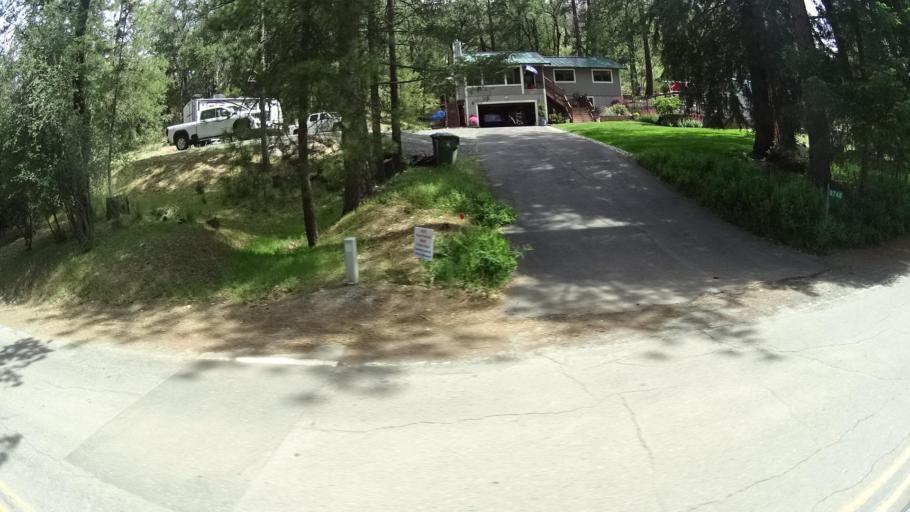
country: US
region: California
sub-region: Lake County
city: Cobb
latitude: 38.8538
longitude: -122.7291
